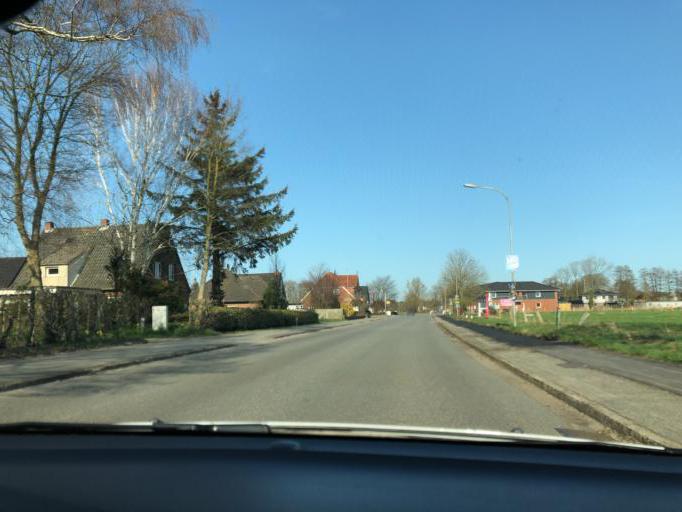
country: DE
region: Schleswig-Holstein
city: Bargum
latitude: 54.6864
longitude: 8.9504
